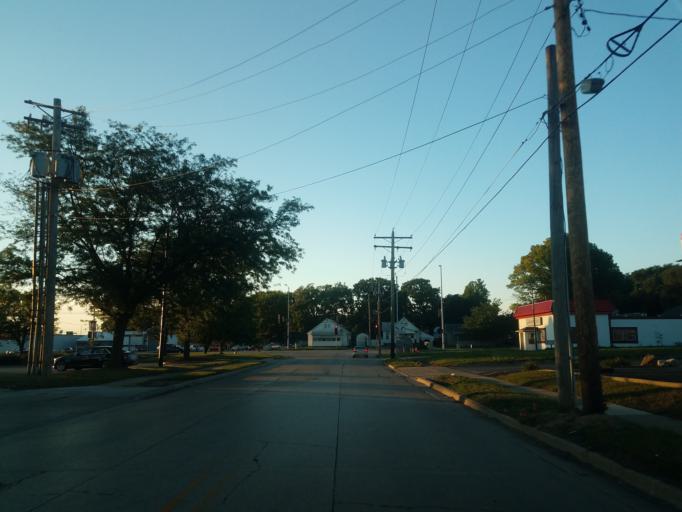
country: US
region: Illinois
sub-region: McLean County
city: Bloomington
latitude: 40.4823
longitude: -89.0159
